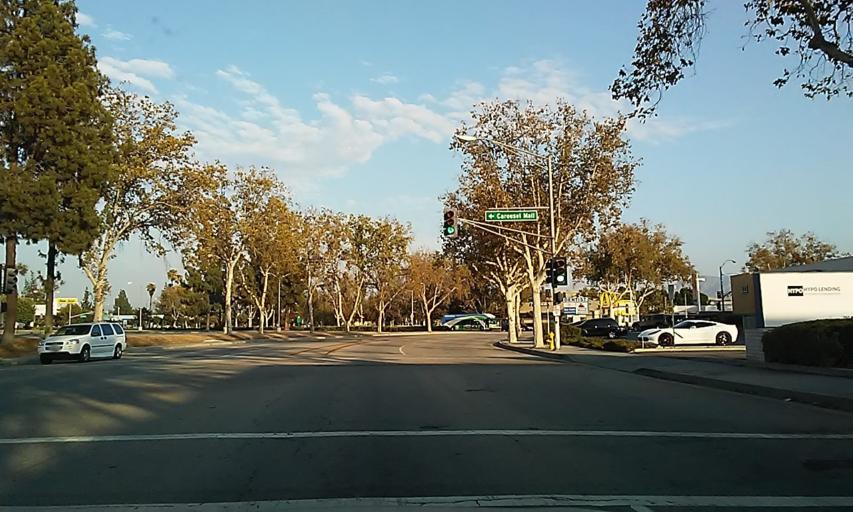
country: US
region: California
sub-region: San Bernardino County
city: San Bernardino
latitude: 34.1038
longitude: -117.2993
